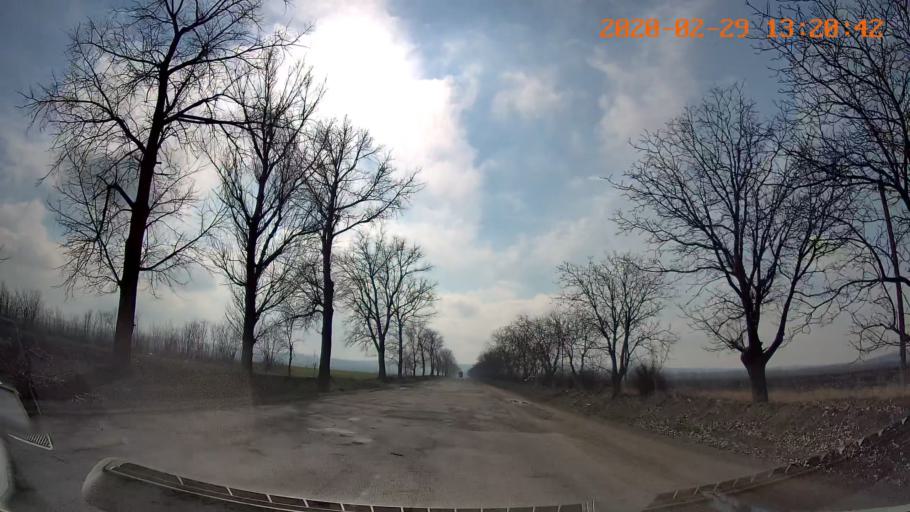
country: MD
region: Telenesti
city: Camenca
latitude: 47.9765
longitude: 28.6390
